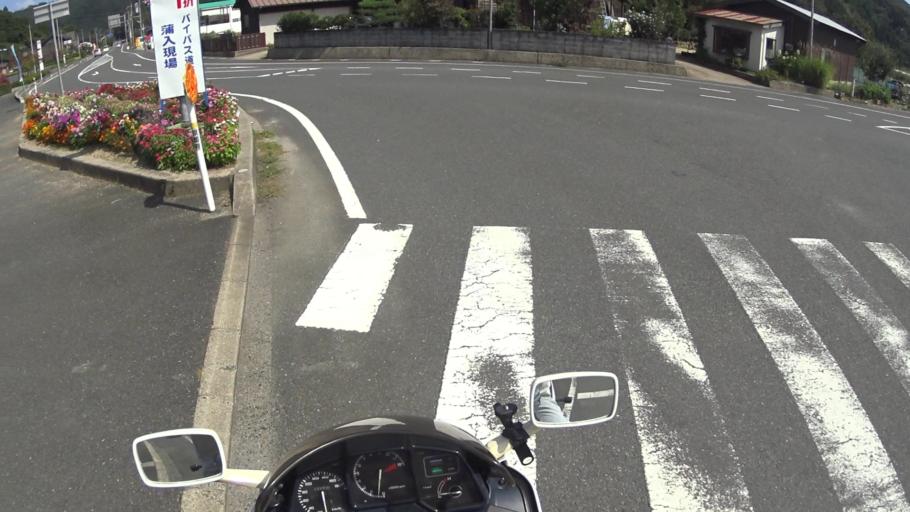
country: JP
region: Kyoto
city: Miyazu
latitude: 35.7206
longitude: 135.2526
